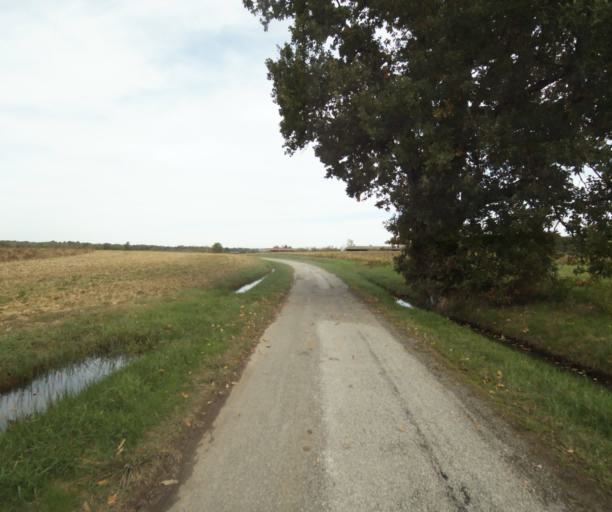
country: FR
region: Midi-Pyrenees
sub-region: Departement de la Haute-Garonne
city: Fronton
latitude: 43.8732
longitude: 1.3885
